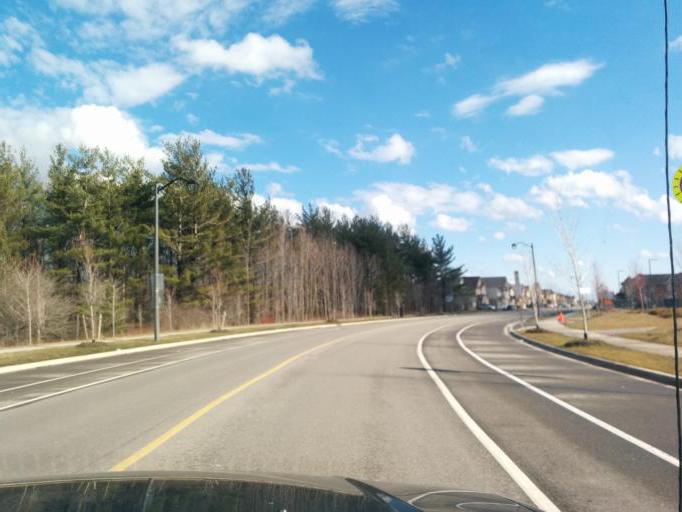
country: CA
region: Ontario
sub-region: Halton
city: Milton
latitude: 43.4970
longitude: -79.8617
